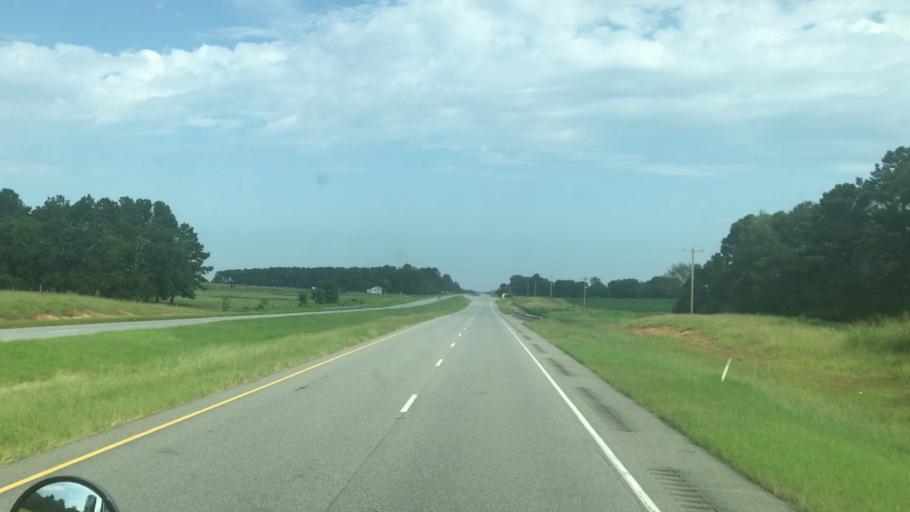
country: US
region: Georgia
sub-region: Early County
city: Blakely
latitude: 31.3132
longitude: -84.8741
